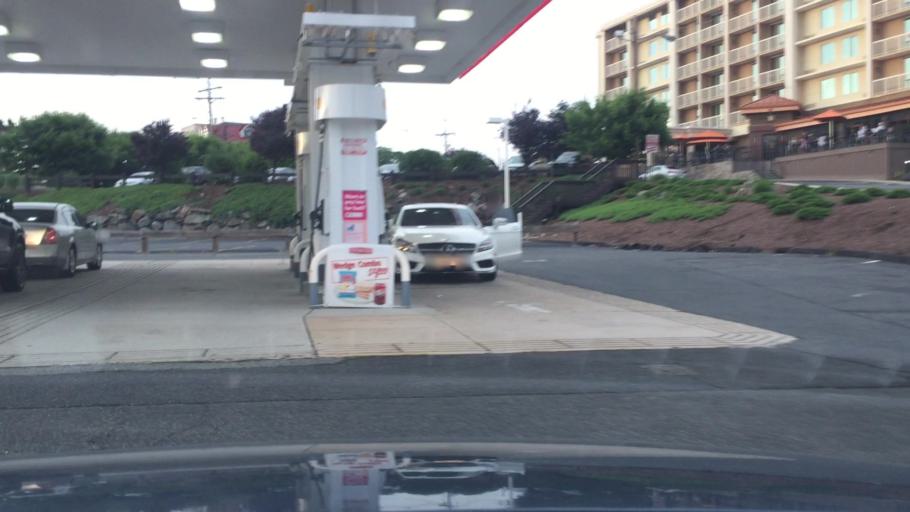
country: US
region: Massachusetts
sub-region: Middlesex County
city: Waltham
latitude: 42.3971
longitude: -71.2585
